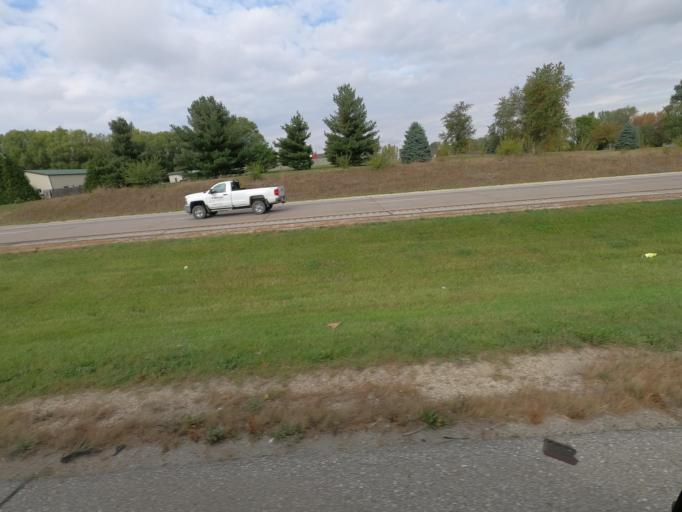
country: US
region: Iowa
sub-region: Polk County
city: Altoona
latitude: 41.5988
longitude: -93.4735
